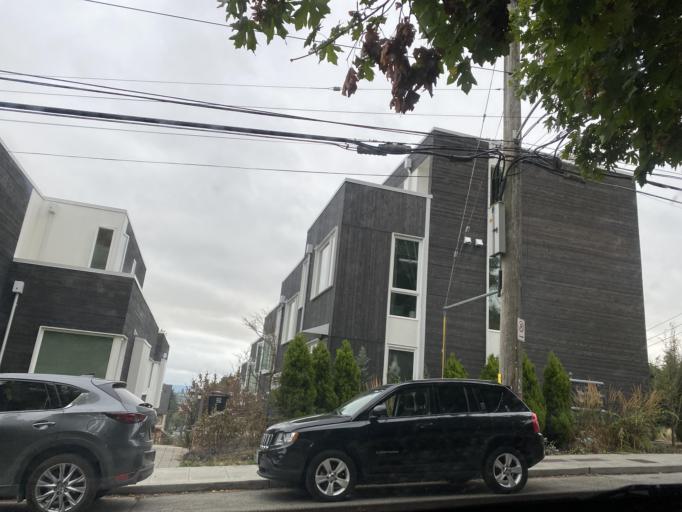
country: US
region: Washington
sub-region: King County
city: Seattle
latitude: 47.6469
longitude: -122.3636
